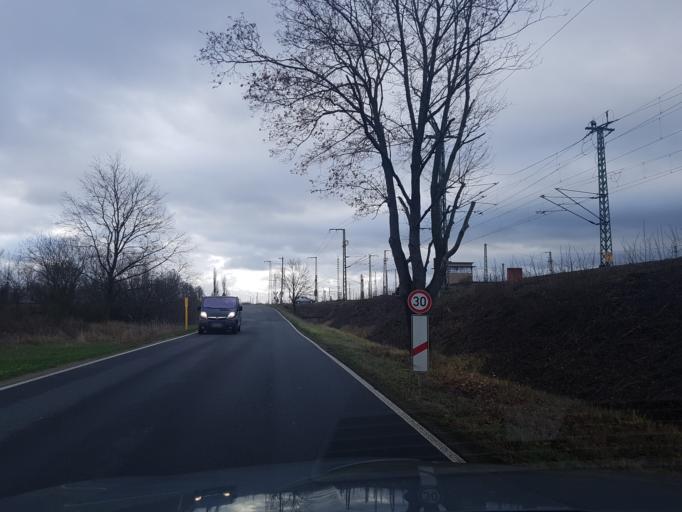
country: DE
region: Brandenburg
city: Falkenberg
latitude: 51.5991
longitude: 13.2420
